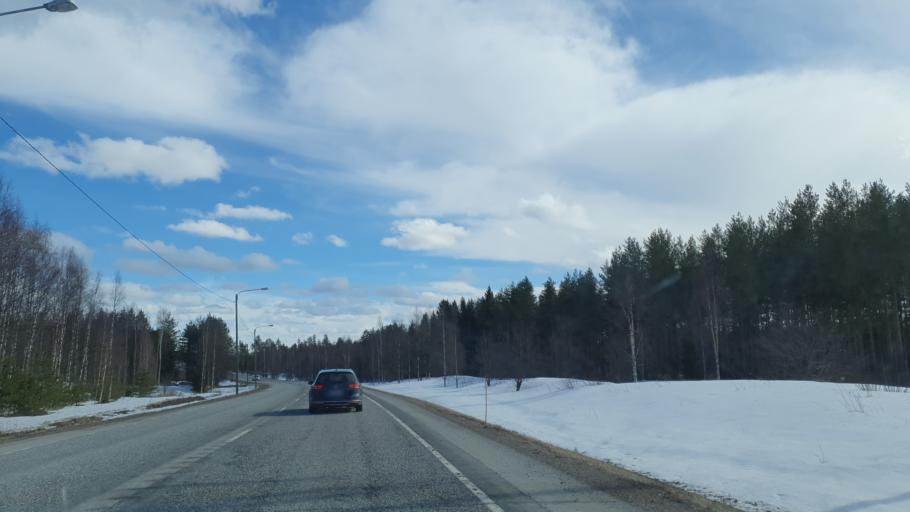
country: FI
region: Kainuu
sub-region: Kajaani
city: Paltamo
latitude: 64.4013
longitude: 27.8723
